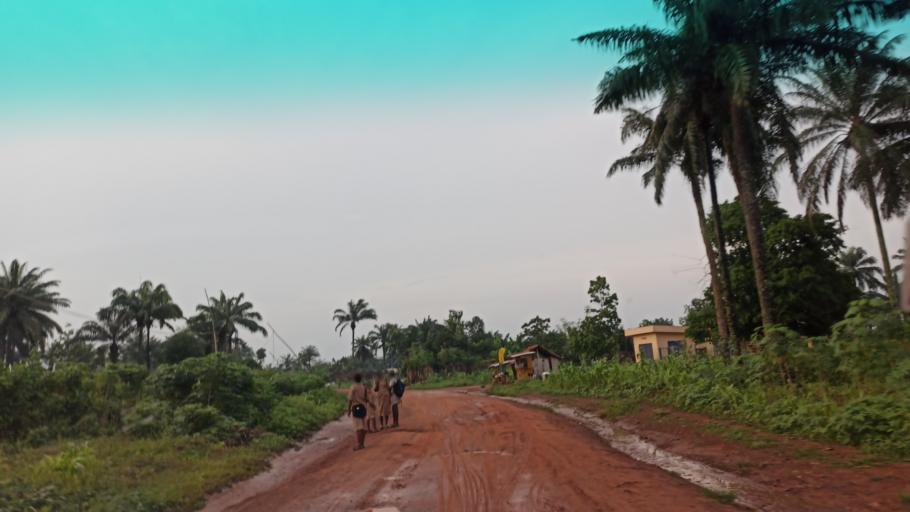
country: BJ
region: Queme
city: Porto-Novo
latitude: 6.5440
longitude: 2.6191
